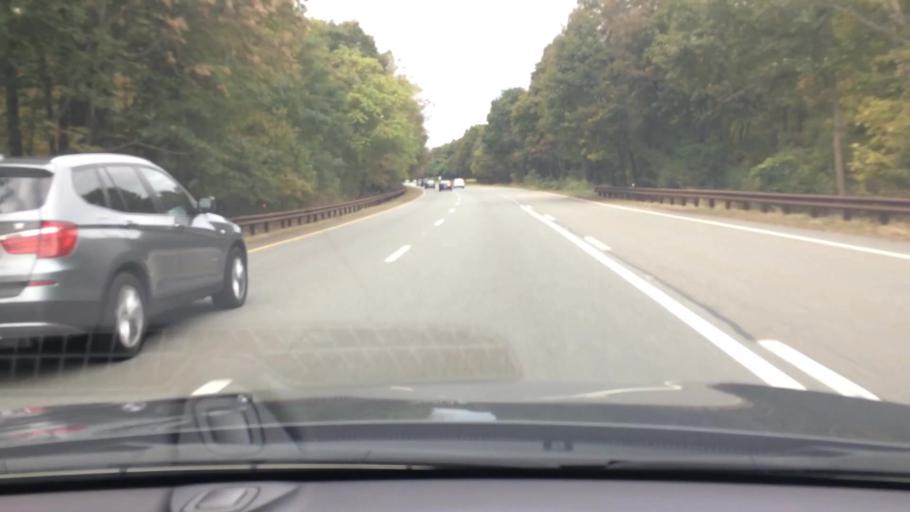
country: US
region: New Jersey
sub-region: Bergen County
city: Alpine
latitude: 40.9586
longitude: -73.9188
